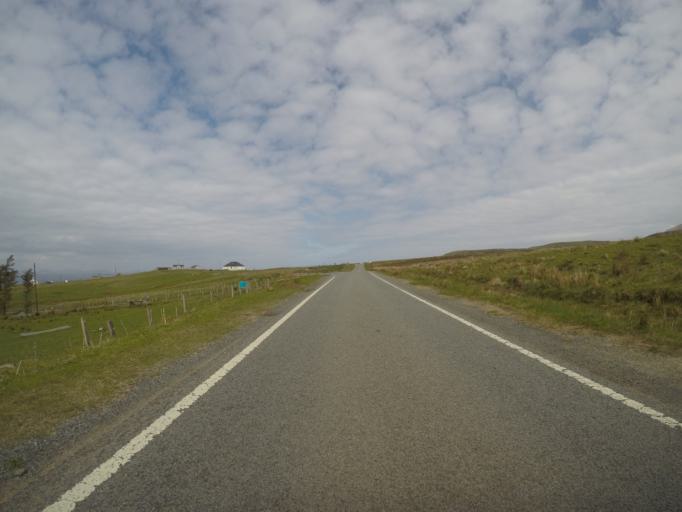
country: GB
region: Scotland
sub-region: Highland
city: Portree
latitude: 57.6539
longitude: -6.3795
